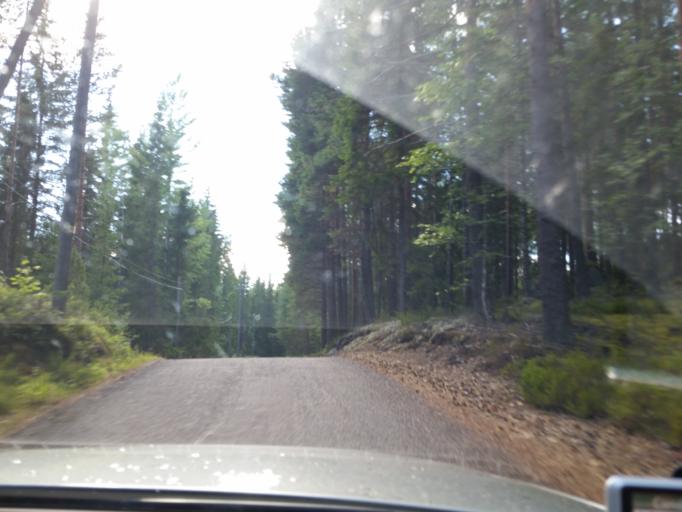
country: FI
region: Uusimaa
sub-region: Helsinki
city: Kaerkoelae
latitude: 60.5557
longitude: 23.9869
